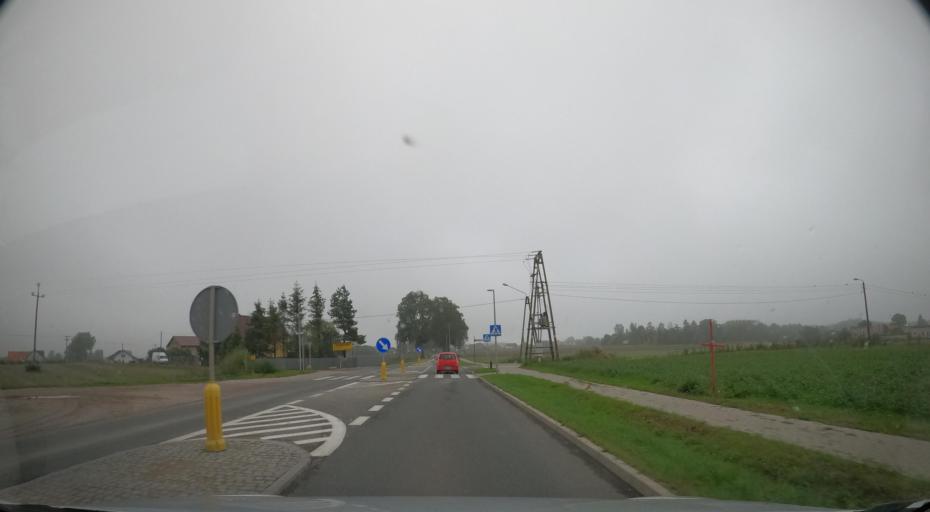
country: PL
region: Pomeranian Voivodeship
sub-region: Powiat wejherowski
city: Bojano
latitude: 54.4515
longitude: 18.3723
